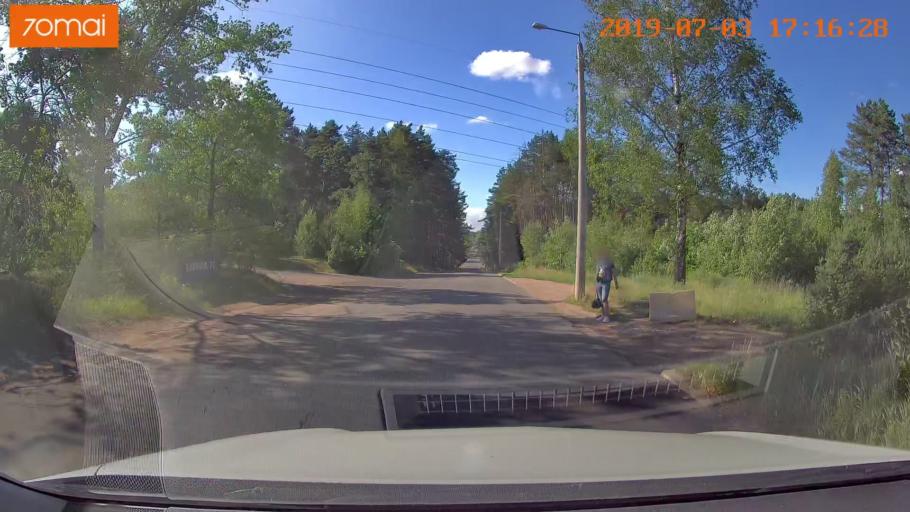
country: BY
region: Minsk
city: Vyaliki Trastsyanets
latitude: 53.9064
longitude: 27.6770
